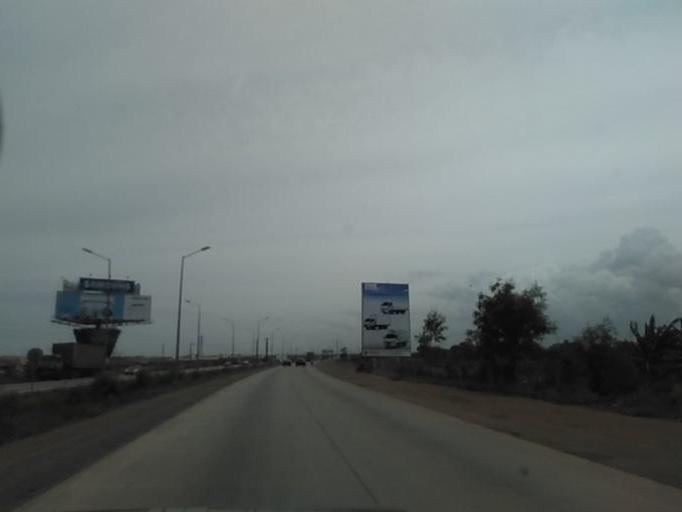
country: GH
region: Greater Accra
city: Nungua
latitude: 5.6607
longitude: -0.0758
